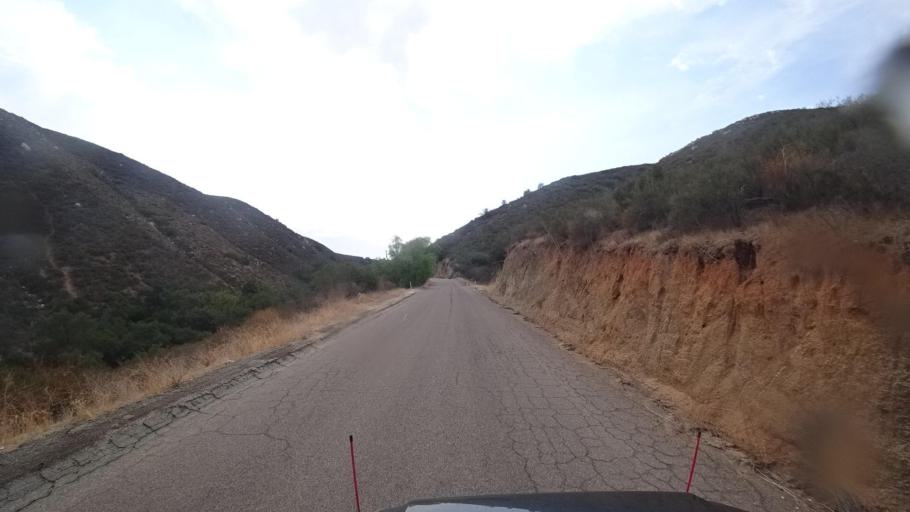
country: US
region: California
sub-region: San Diego County
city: Ramona
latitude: 33.0978
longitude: -116.8585
